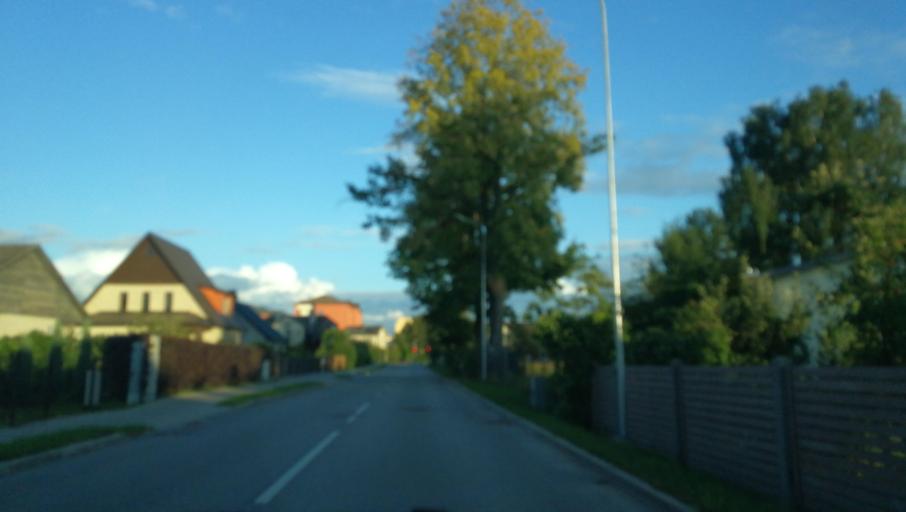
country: LV
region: Valmieras Rajons
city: Valmiera
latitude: 57.5323
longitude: 25.3908
